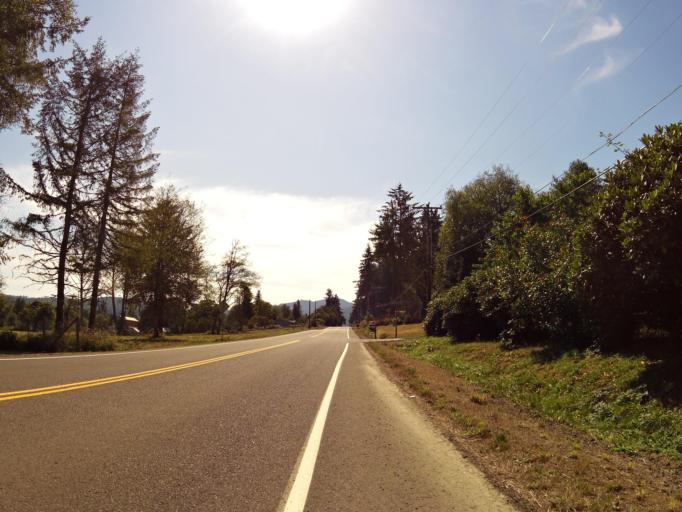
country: US
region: Washington
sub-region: Wahkiakum County
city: Cathlamet
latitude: 46.1795
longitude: -123.5830
